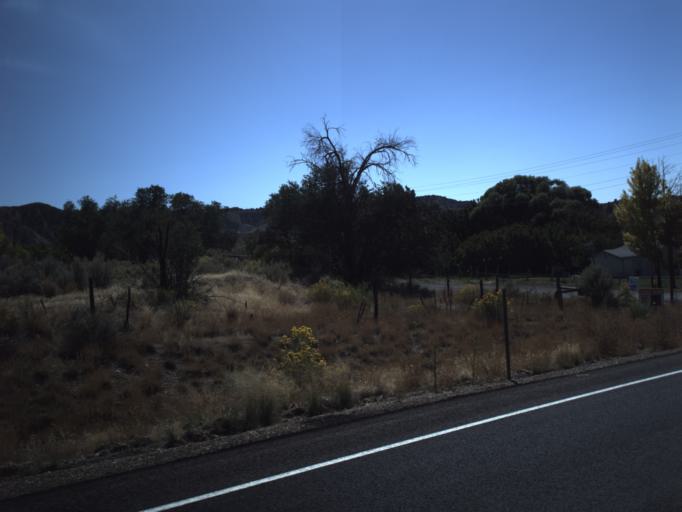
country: US
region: Utah
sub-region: Garfield County
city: Panguitch
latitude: 37.5627
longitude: -111.9925
